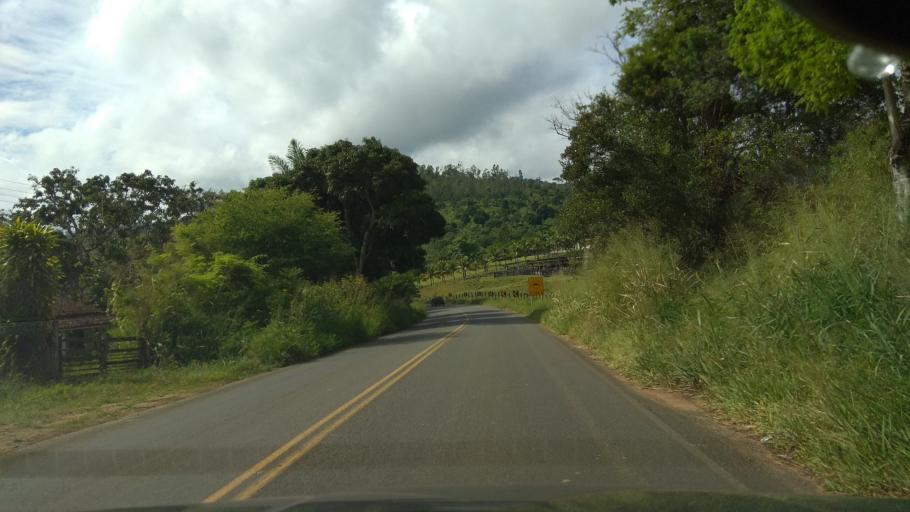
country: BR
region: Bahia
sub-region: Ubaira
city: Ubaira
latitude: -13.2714
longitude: -39.6356
